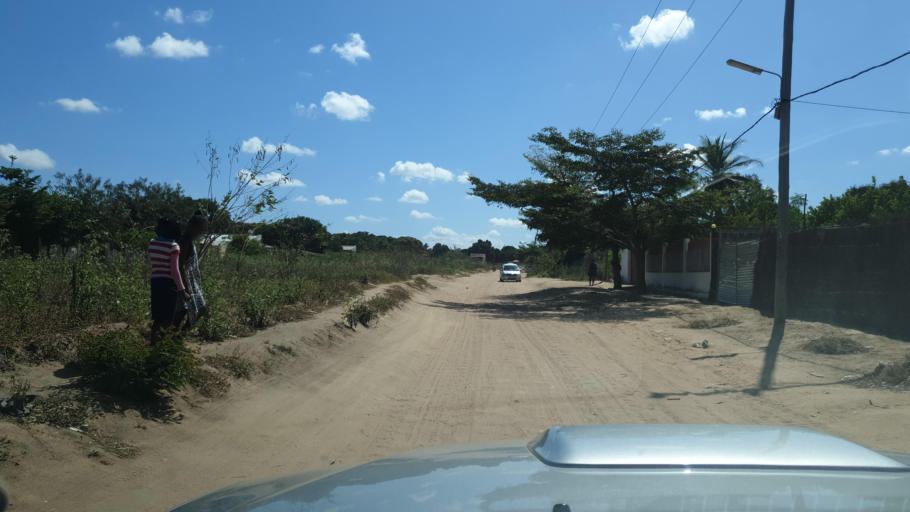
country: MZ
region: Nampula
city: Nampula
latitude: -15.1041
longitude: 39.2060
